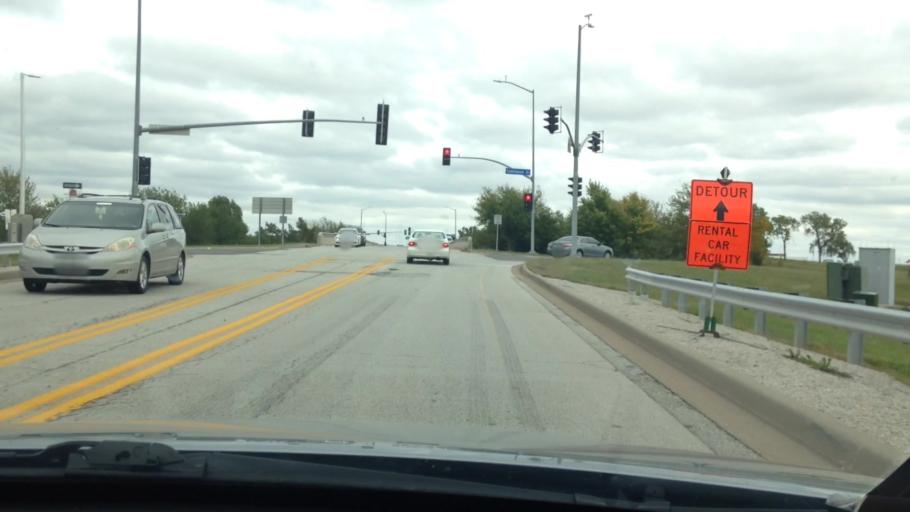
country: US
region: Missouri
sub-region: Platte County
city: Weatherby Lake
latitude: 39.3027
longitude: -94.7151
